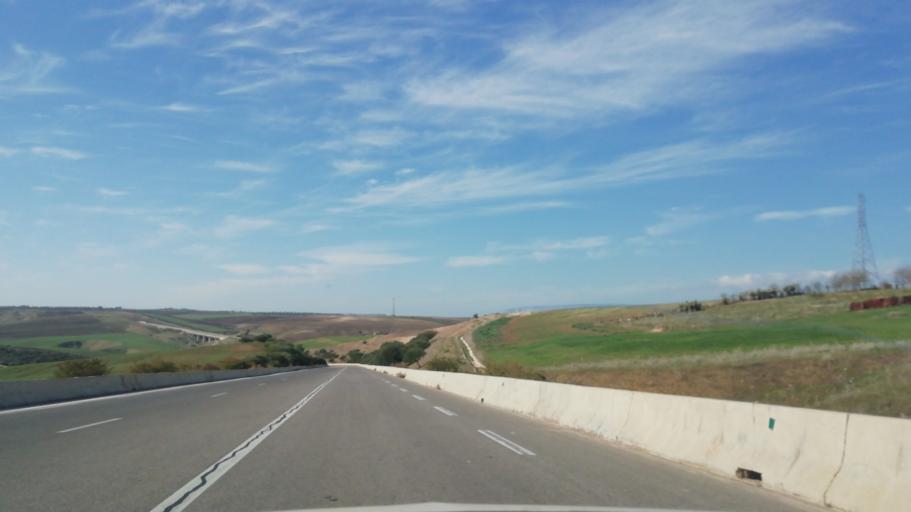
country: DZ
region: Tlemcen
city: Chetouane
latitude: 34.9814
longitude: -1.2247
